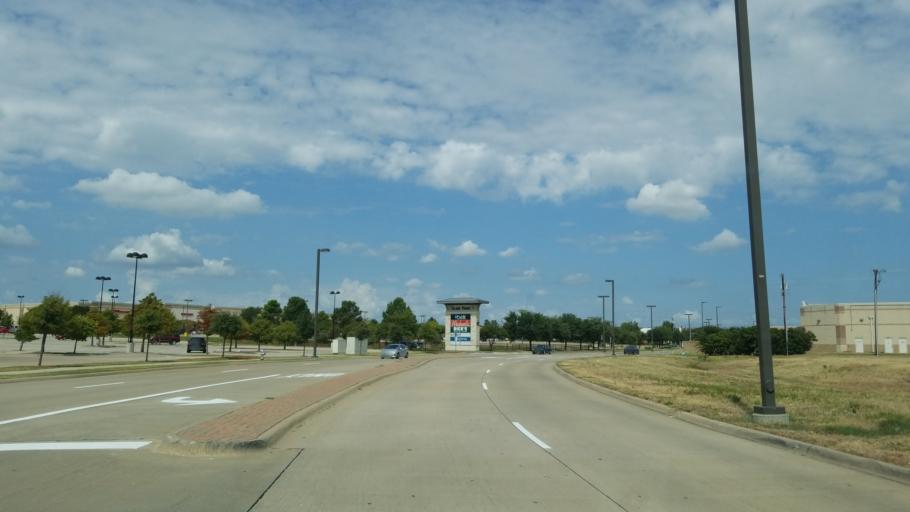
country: US
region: Texas
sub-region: Tarrant County
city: Euless
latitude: 32.8785
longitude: -97.1022
